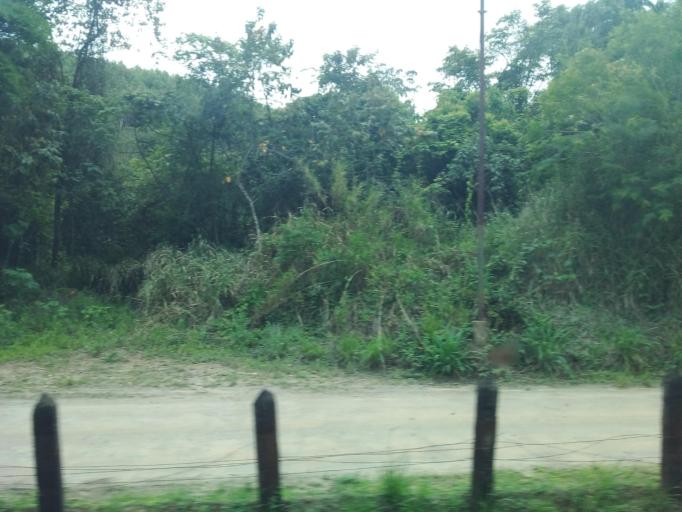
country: BR
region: Minas Gerais
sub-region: Nova Era
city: Nova Era
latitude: -19.7251
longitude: -42.9859
